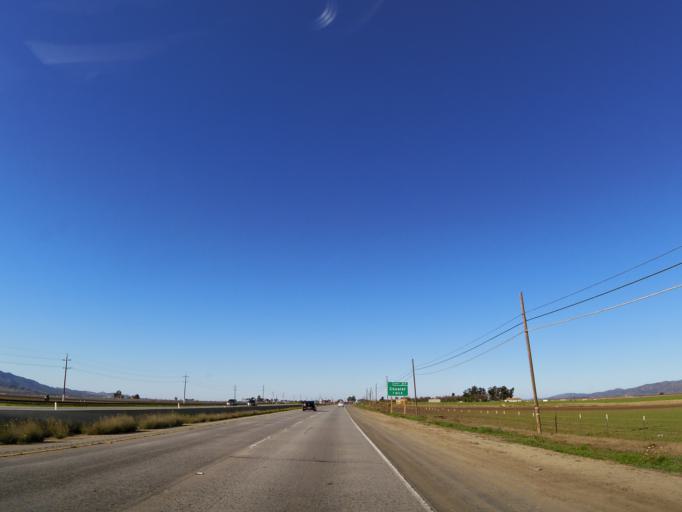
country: US
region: California
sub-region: Monterey County
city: Chualar
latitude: 36.5545
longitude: -121.5026
